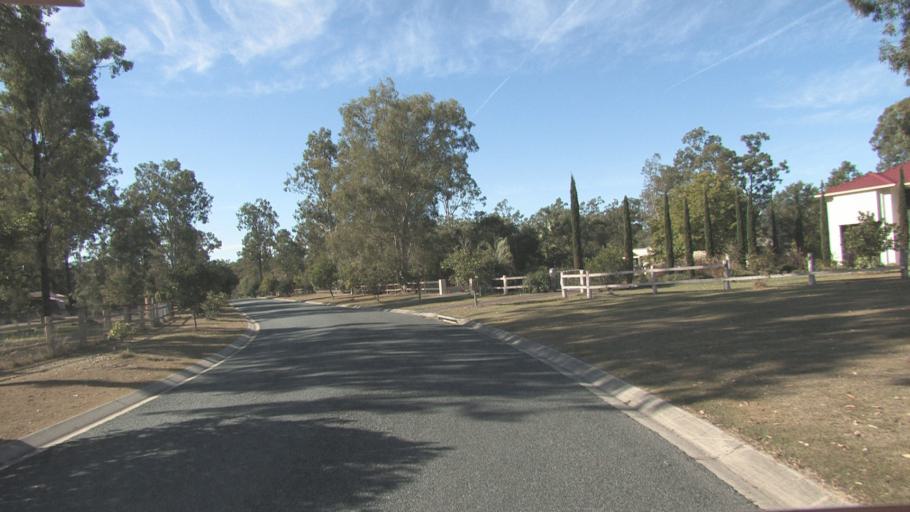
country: AU
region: Queensland
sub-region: Logan
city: North Maclean
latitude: -27.8085
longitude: 152.9641
